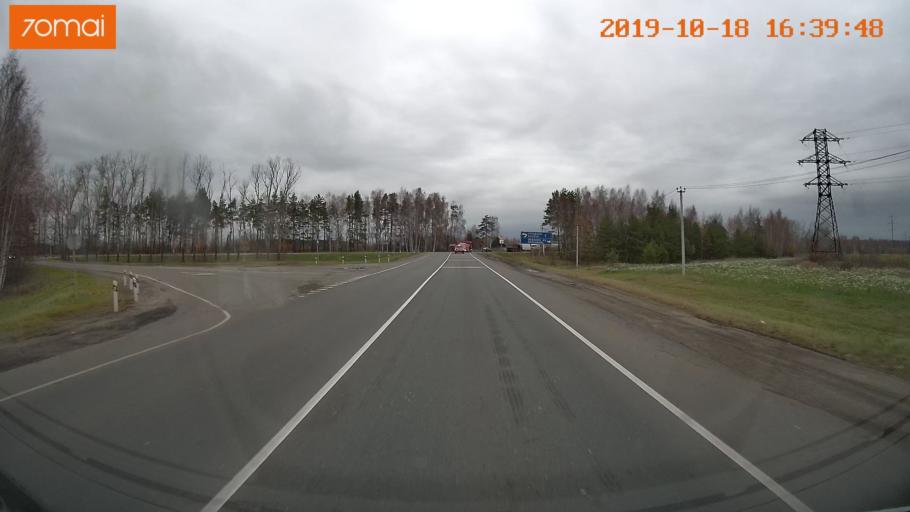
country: RU
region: Vladimir
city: Suzdal'
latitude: 56.4555
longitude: 40.4596
